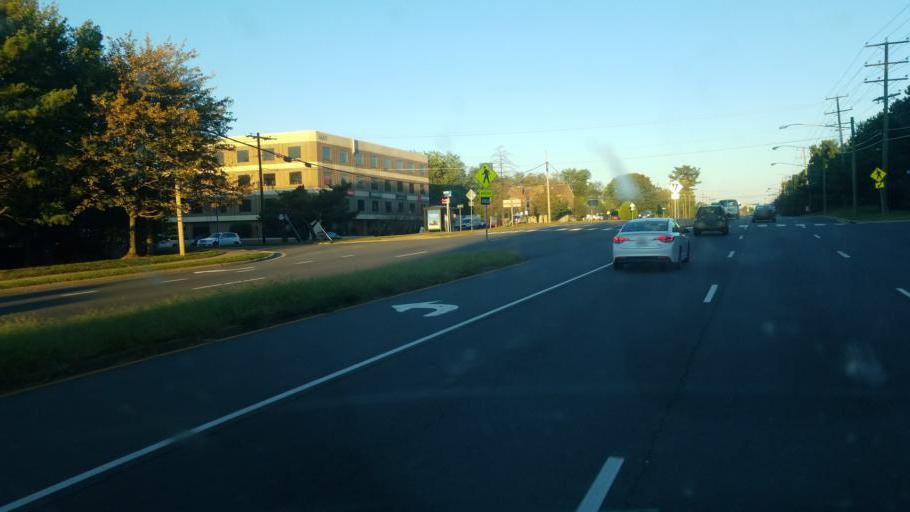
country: US
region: Virginia
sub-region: Fairfax County
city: Lincolnia
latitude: 38.8234
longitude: -77.1658
